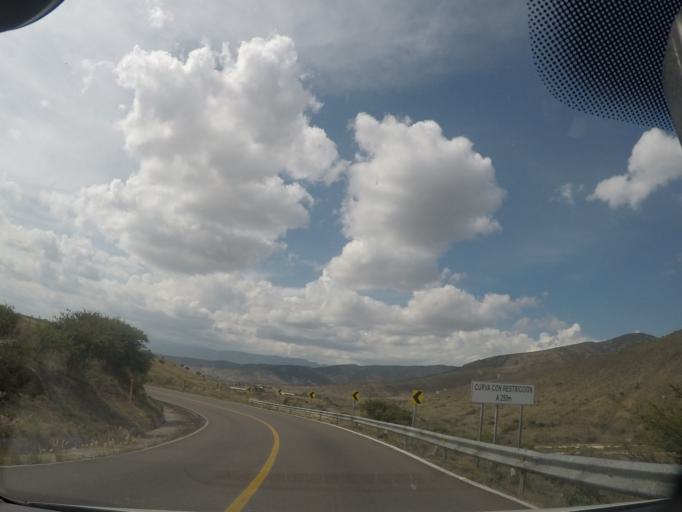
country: MX
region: Oaxaca
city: Santiago Matatlan
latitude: 16.8398
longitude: -96.3705
